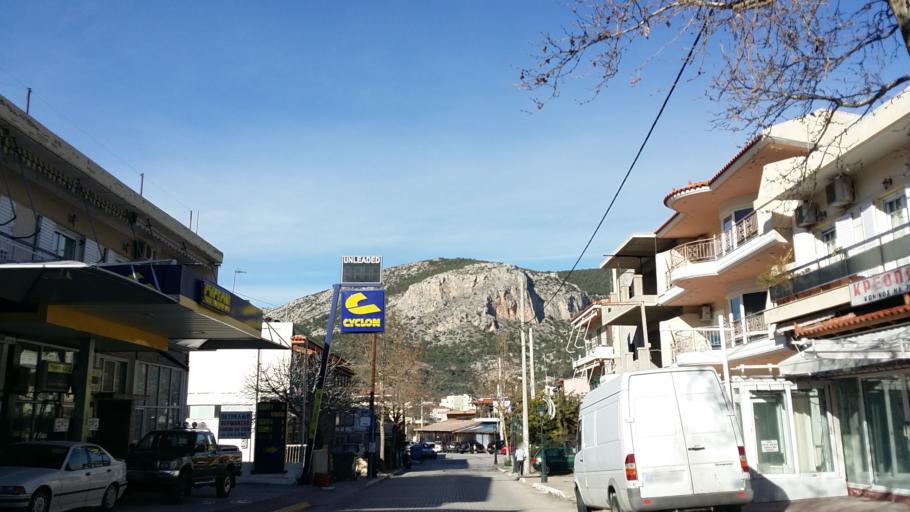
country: GR
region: Attica
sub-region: Nomarchia Dytikis Attikis
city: Fyli
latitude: 38.1042
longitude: 23.6690
